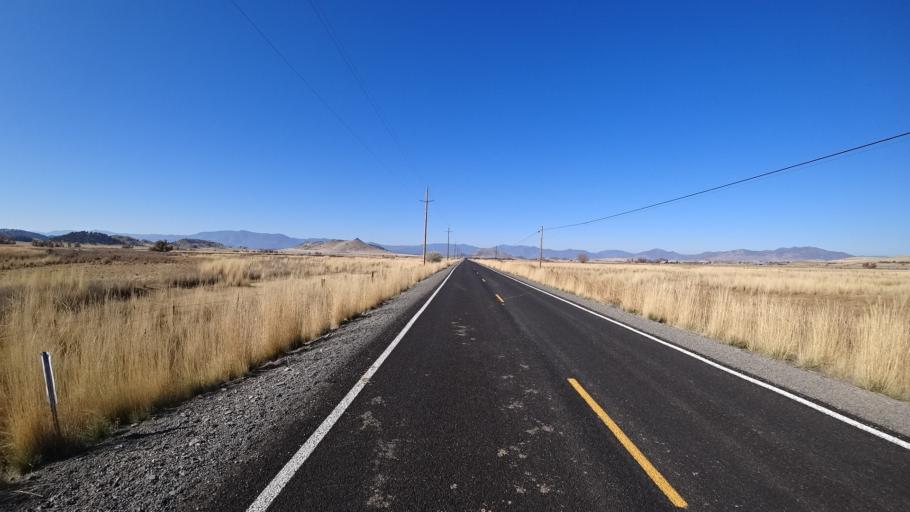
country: US
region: California
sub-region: Siskiyou County
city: Montague
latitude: 41.7114
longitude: -122.4237
